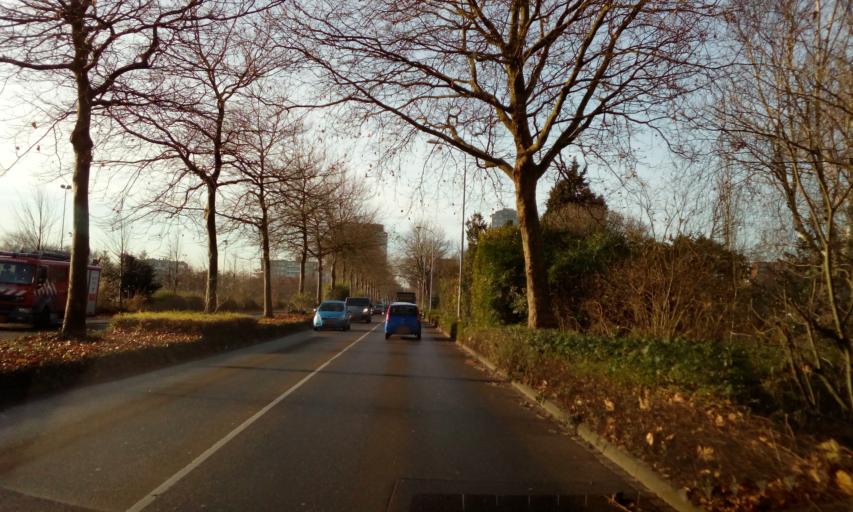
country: NL
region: South Holland
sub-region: Gemeente Leidschendam-Voorburg
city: Voorburg
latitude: 52.0777
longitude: 4.3665
